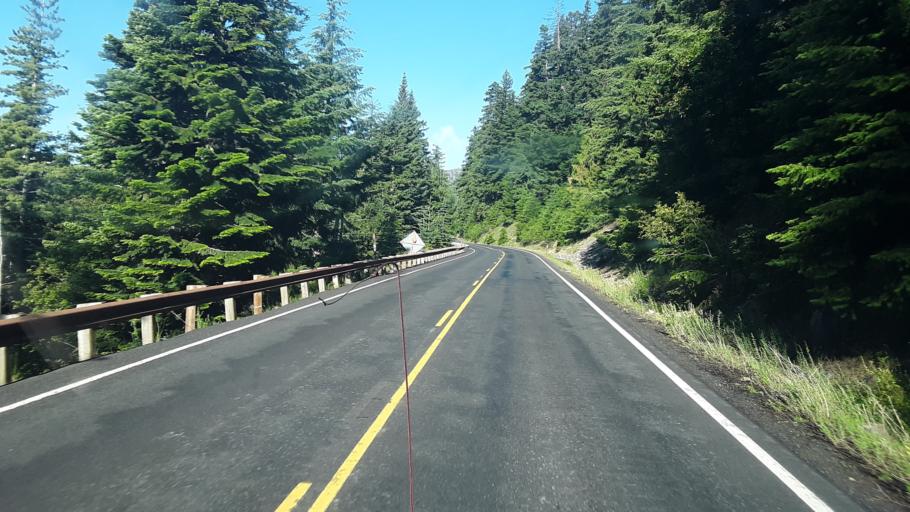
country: US
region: Washington
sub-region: Kittitas County
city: Cle Elum
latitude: 46.8967
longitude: -121.4610
